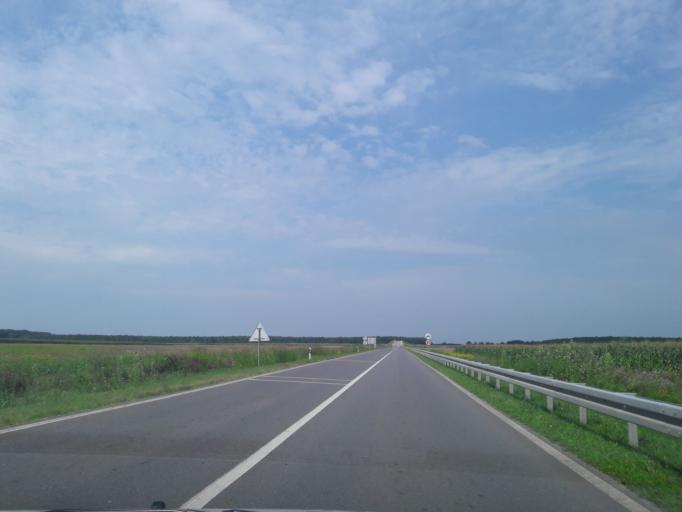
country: HR
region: Osjecko-Baranjska
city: Cepin
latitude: 45.5159
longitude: 18.5206
